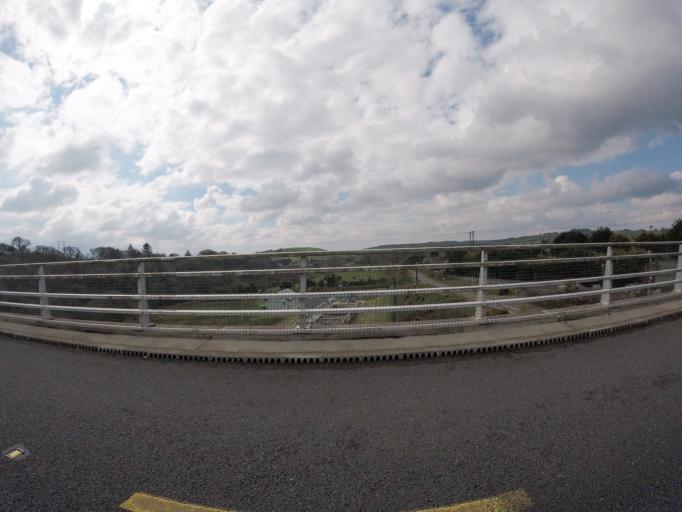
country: IE
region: Leinster
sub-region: Kilkenny
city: Mooncoin
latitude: 52.2387
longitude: -7.2387
